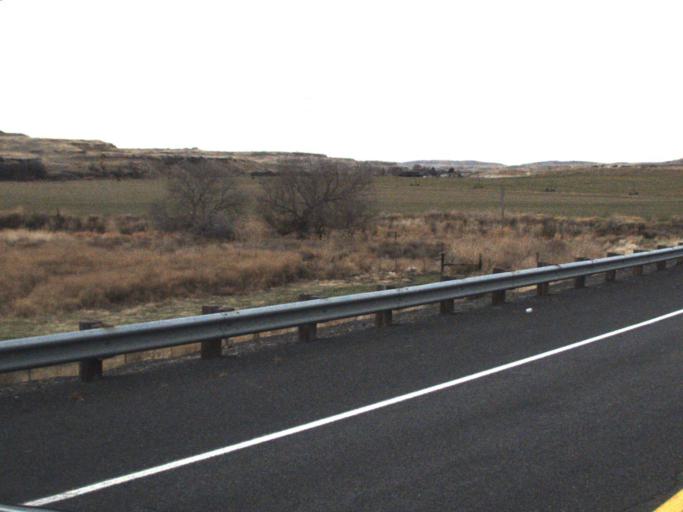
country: US
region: Washington
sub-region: Columbia County
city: Dayton
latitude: 46.7732
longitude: -118.0405
